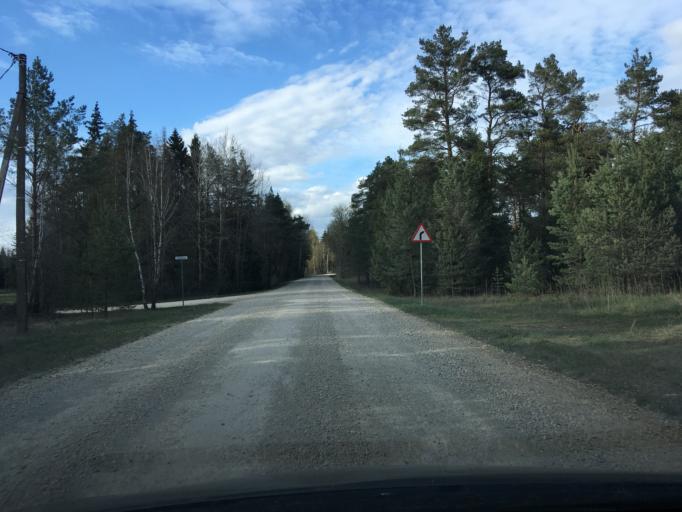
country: EE
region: Raplamaa
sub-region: Maerjamaa vald
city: Marjamaa
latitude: 58.9672
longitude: 24.3317
